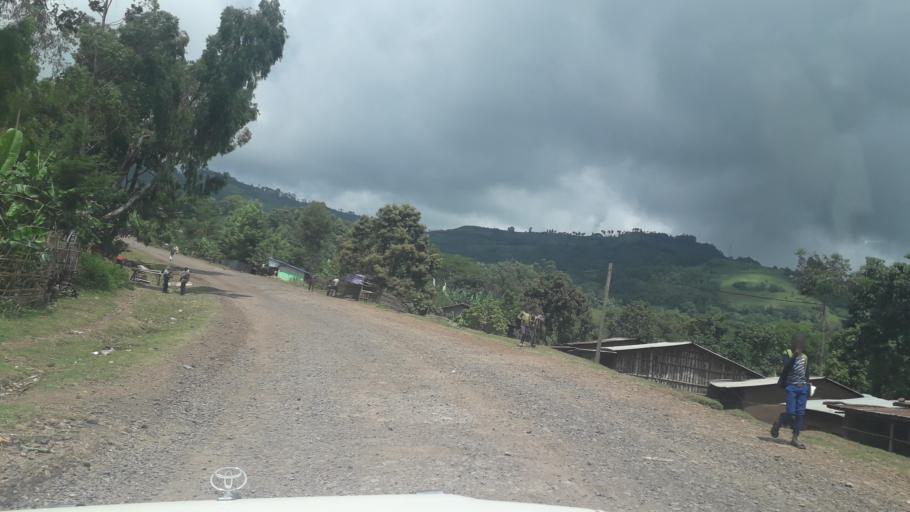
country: ET
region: Oromiya
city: Jima
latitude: 7.4234
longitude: 36.8731
